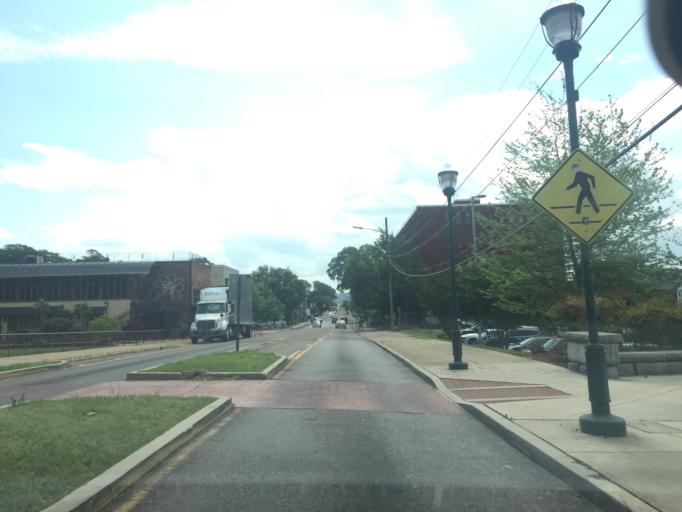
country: US
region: Tennessee
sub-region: Hamilton County
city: Chattanooga
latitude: 35.0444
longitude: -85.2976
